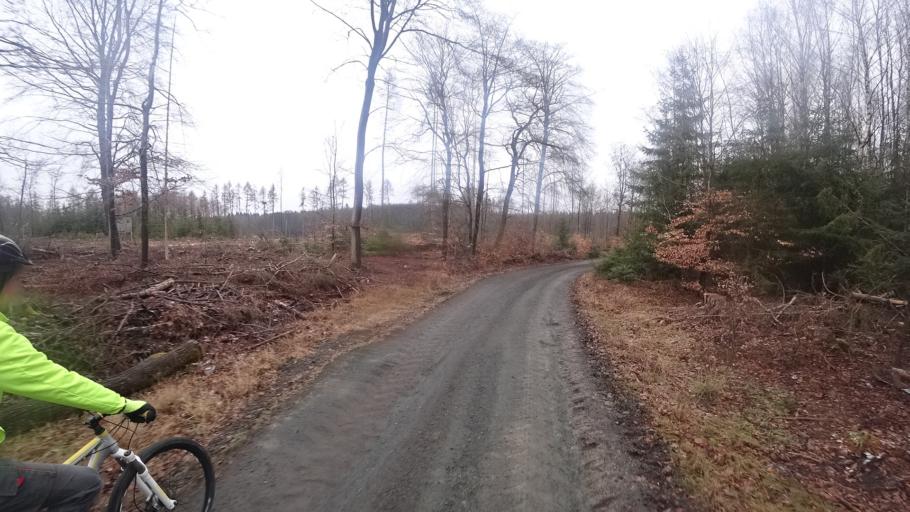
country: DE
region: Rheinland-Pfalz
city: Weidenbach
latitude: 50.1480
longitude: 7.9139
